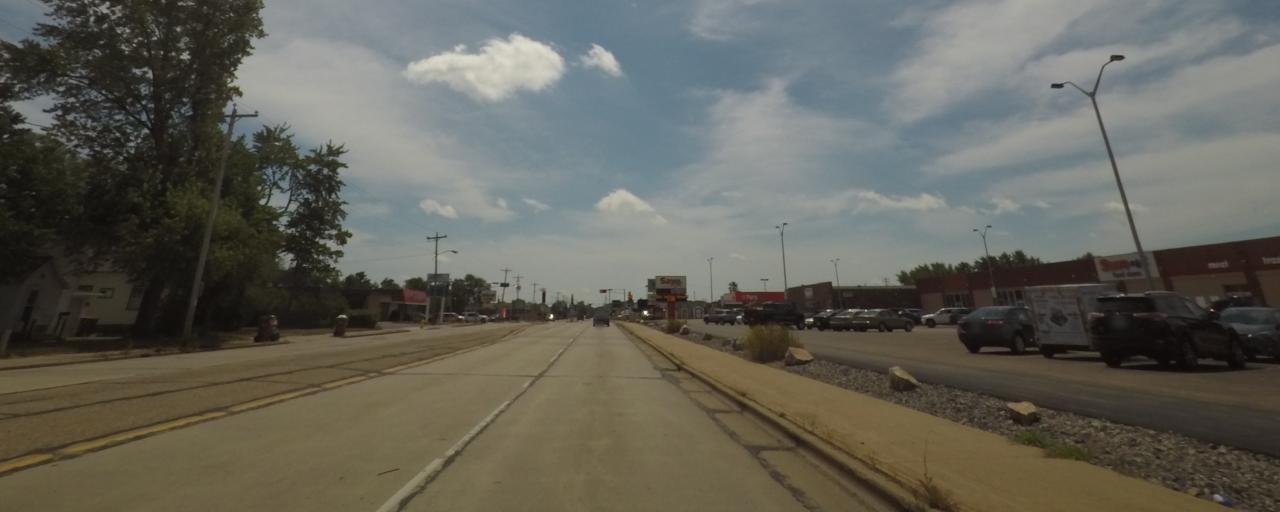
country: US
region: Wisconsin
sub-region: Portage County
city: Whiting
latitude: 44.5036
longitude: -89.5662
